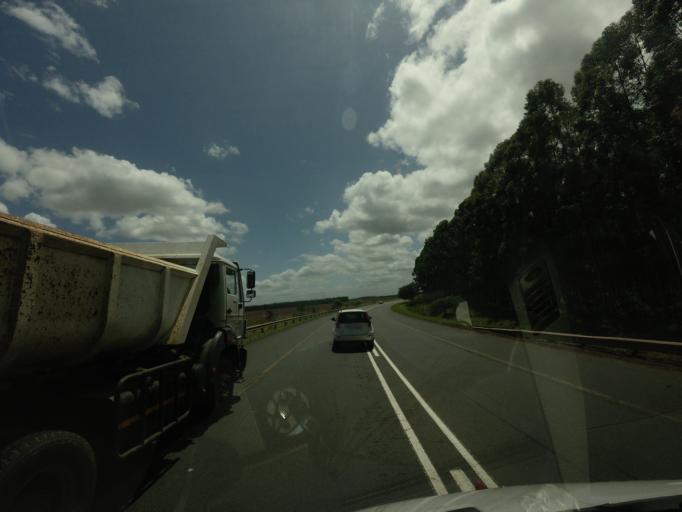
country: ZA
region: KwaZulu-Natal
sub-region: uThungulu District Municipality
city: KwaMbonambi
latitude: -28.5809
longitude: 32.0993
